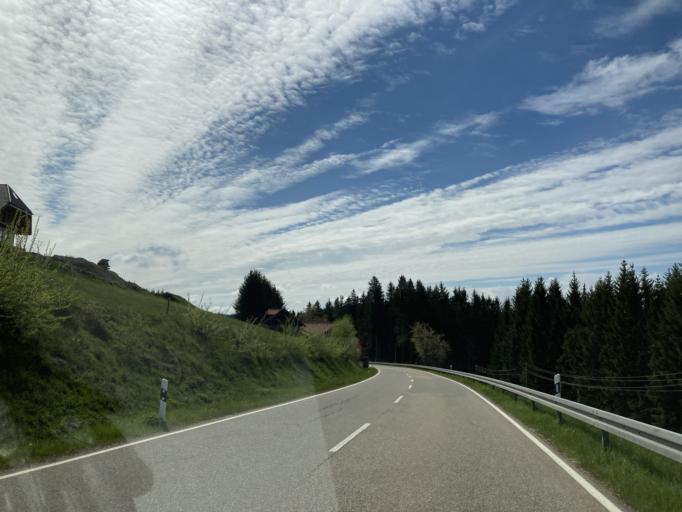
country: DE
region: Baden-Wuerttemberg
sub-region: Freiburg Region
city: Schonwald im Schwarzwald
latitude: 48.0847
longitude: 8.2009
